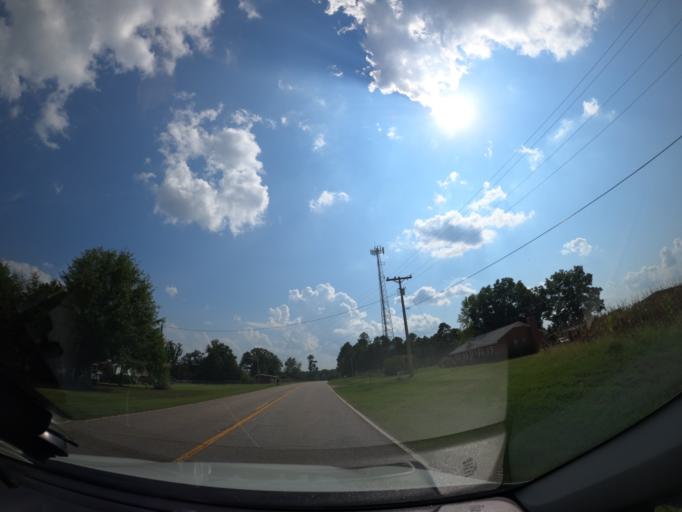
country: US
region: South Carolina
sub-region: Barnwell County
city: Williston
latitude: 33.6064
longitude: -81.4429
